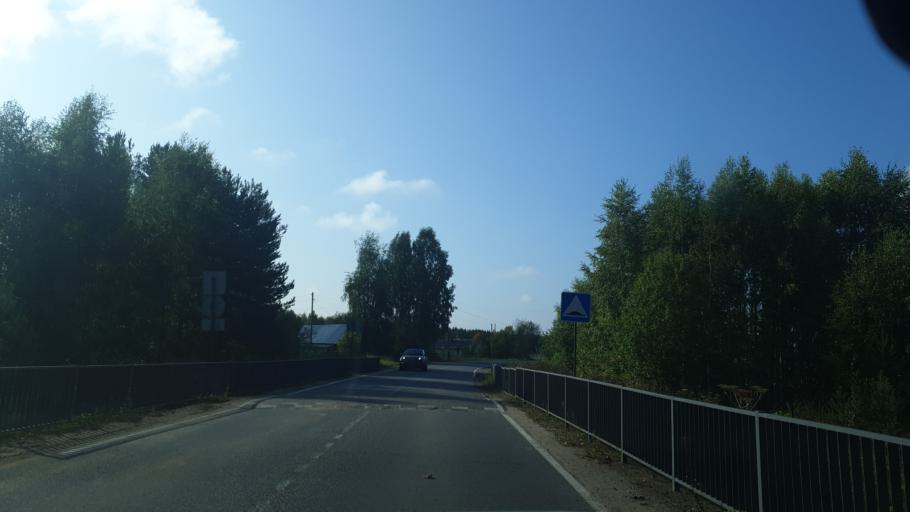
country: RU
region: Komi Republic
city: Vizinga
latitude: 60.9161
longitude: 50.2118
